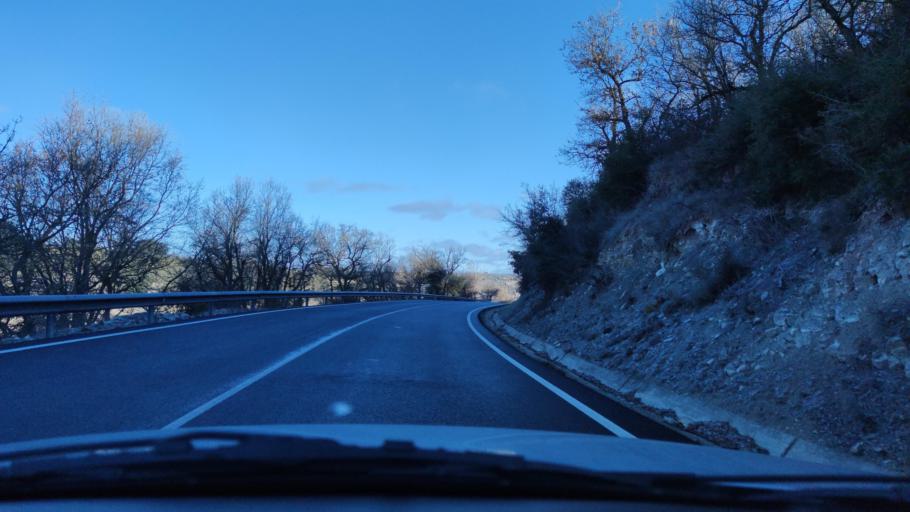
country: ES
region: Catalonia
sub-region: Provincia de Lleida
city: Cervera
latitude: 41.6876
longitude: 1.3053
